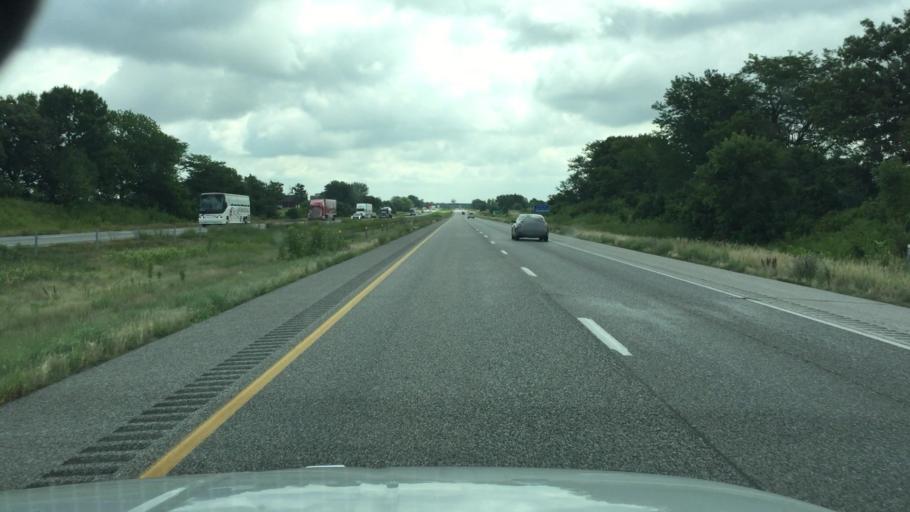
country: US
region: Illinois
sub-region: Rock Island County
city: Hampton
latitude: 41.5971
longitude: -90.4048
